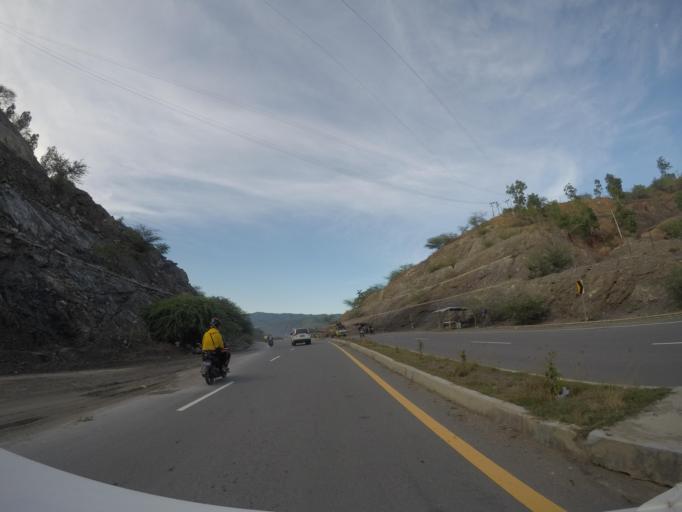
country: TL
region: Dili
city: Dili
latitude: -8.5614
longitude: 125.4933
